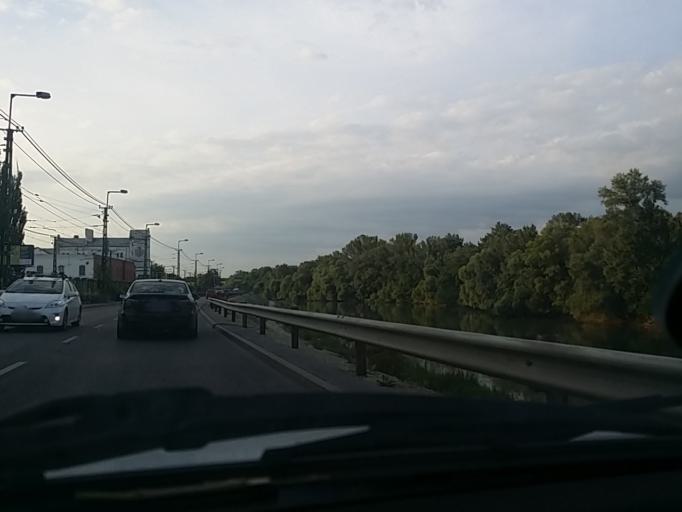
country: HU
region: Budapest
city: Budapest III. keruelet
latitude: 47.5453
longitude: 19.0470
